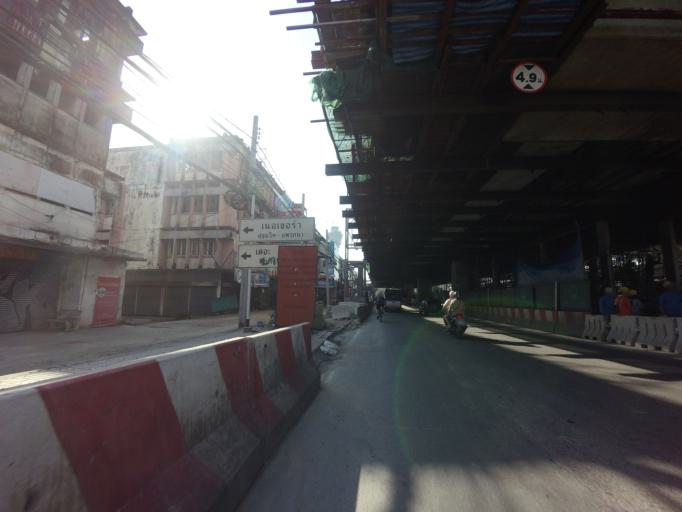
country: TH
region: Samut Prakan
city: Samut Prakan
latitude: 13.6028
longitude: 100.5970
